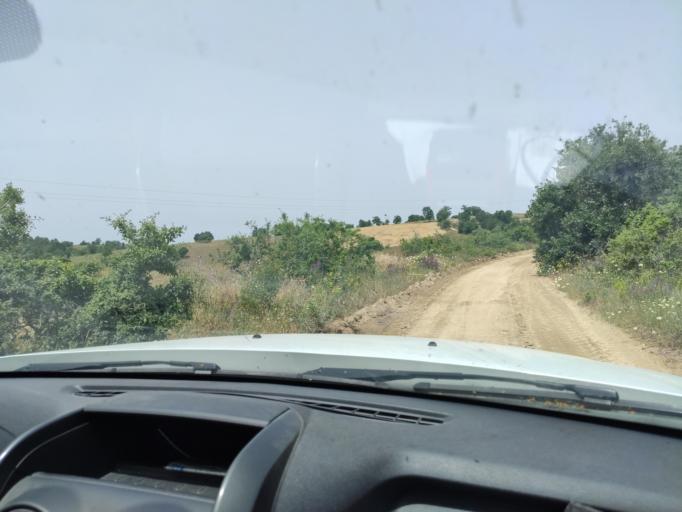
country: MK
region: Radovis
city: Radovish
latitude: 41.6746
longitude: 22.4038
